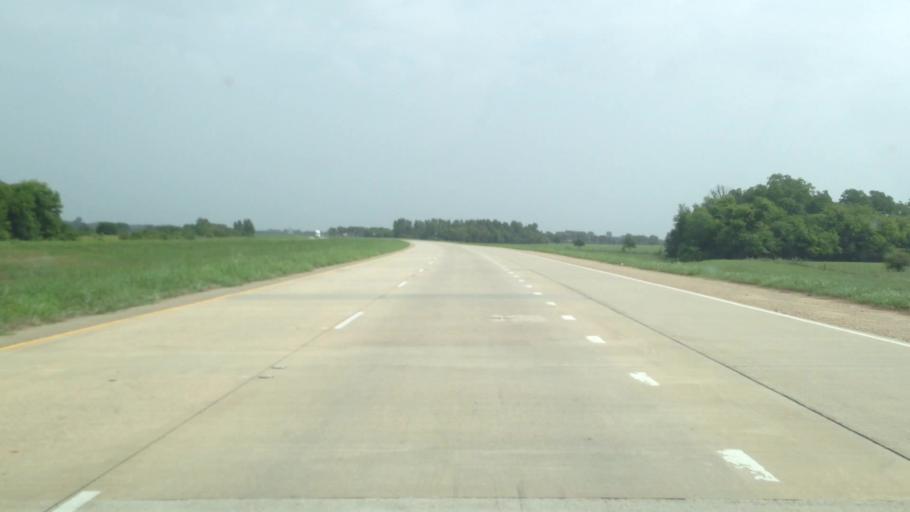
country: US
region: Louisiana
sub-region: Caddo Parish
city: Vivian
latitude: 32.8573
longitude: -93.8617
